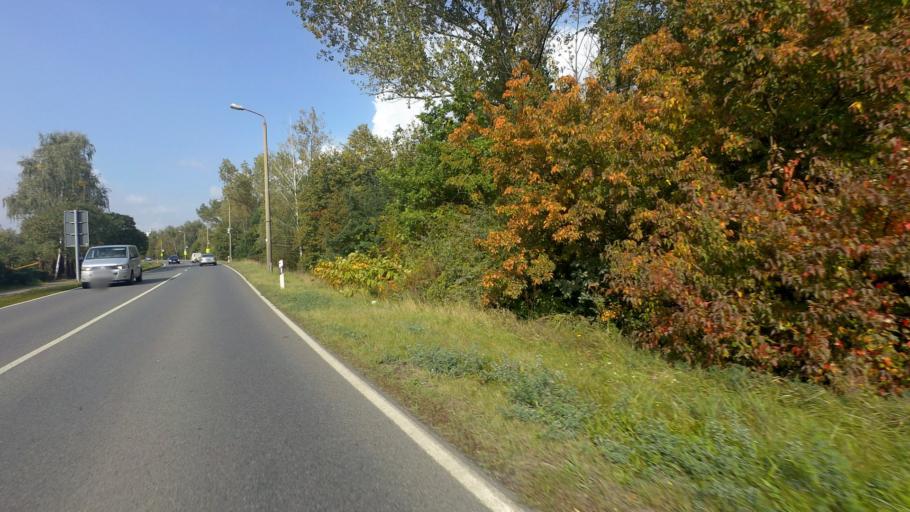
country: DE
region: Brandenburg
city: Elsterwerda
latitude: 51.4644
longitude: 13.5122
